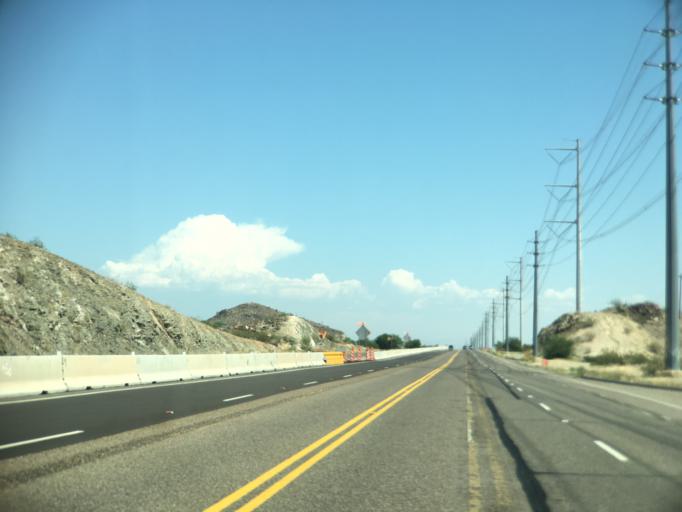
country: US
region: Arizona
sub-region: Maricopa County
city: Guadalupe
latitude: 33.2913
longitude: -112.0554
